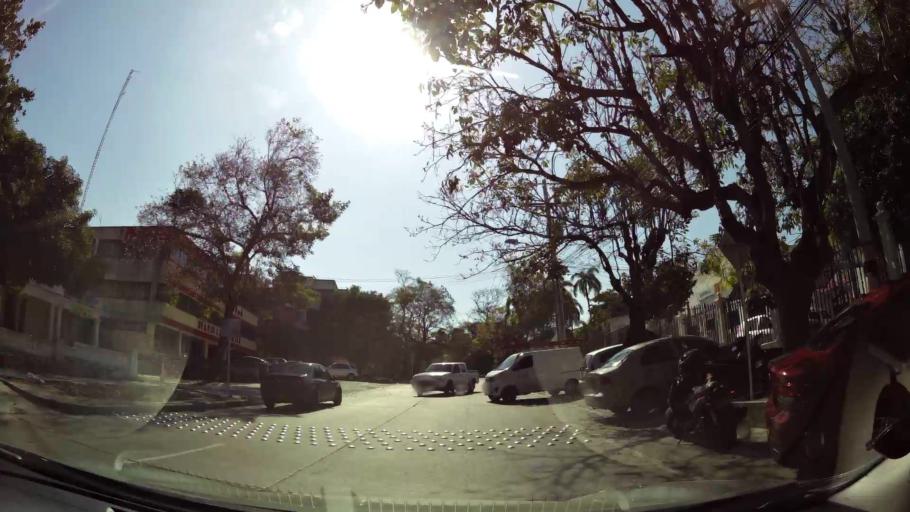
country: CO
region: Atlantico
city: Barranquilla
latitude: 10.9925
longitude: -74.7929
